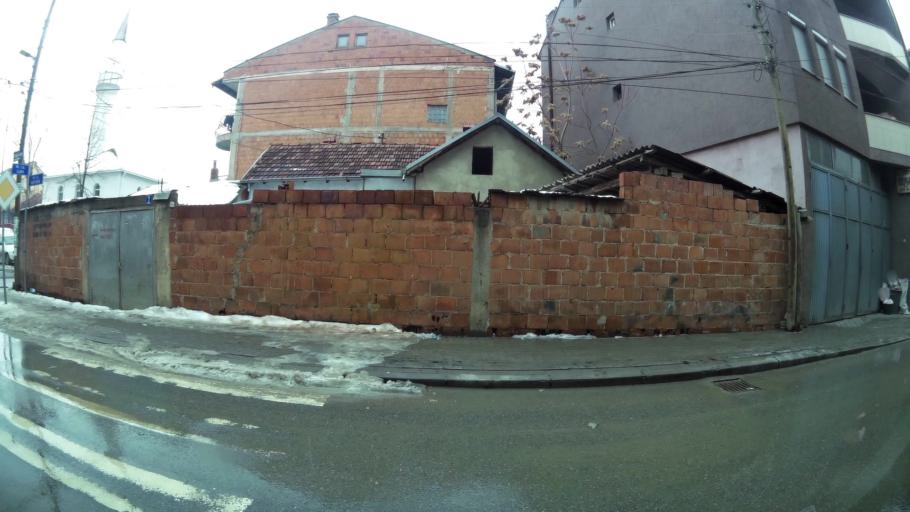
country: XK
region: Pristina
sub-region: Komuna e Prishtines
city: Pristina
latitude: 42.6710
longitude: 21.1691
